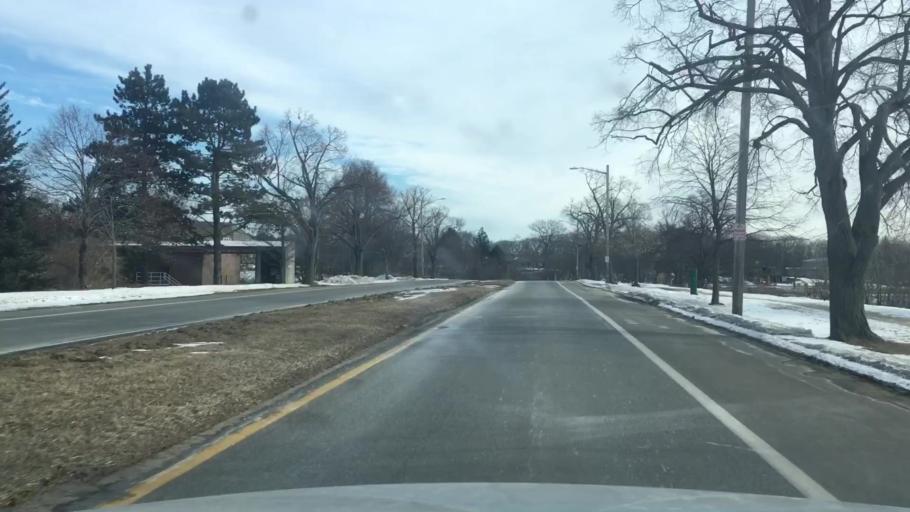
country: US
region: Maine
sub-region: Cumberland County
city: Portland
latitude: 43.6782
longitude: -70.2739
